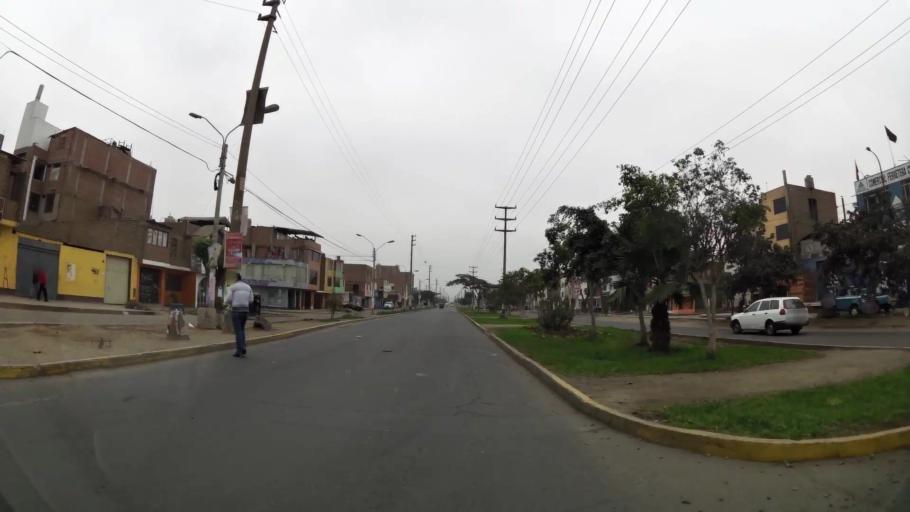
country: PE
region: Lima
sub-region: Lima
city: Urb. Santo Domingo
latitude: -11.8987
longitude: -77.0318
